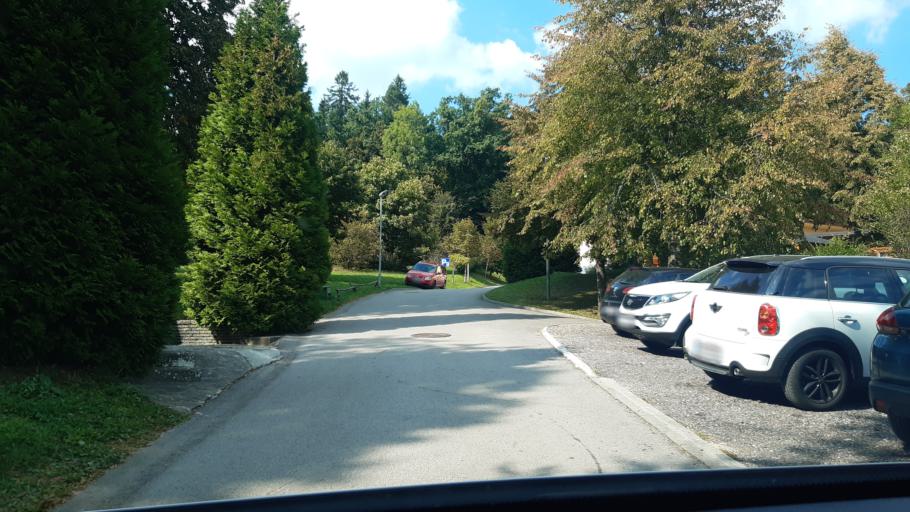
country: SI
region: Lukovica
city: Lukovica pri Domzalah
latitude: 46.1701
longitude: 14.6858
